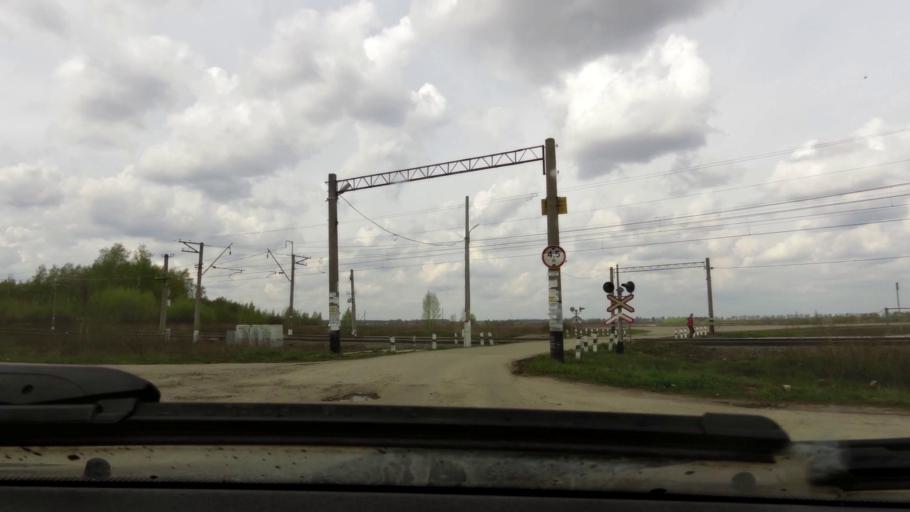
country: RU
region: Rjazan
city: Bagramovo
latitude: 54.7069
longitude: 39.3148
